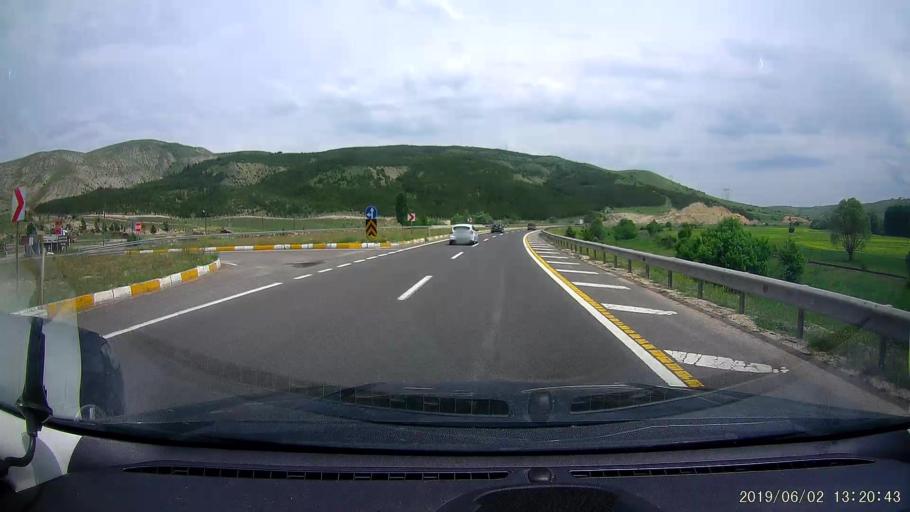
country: TR
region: Cankiri
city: Cerkes
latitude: 40.8421
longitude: 32.7658
